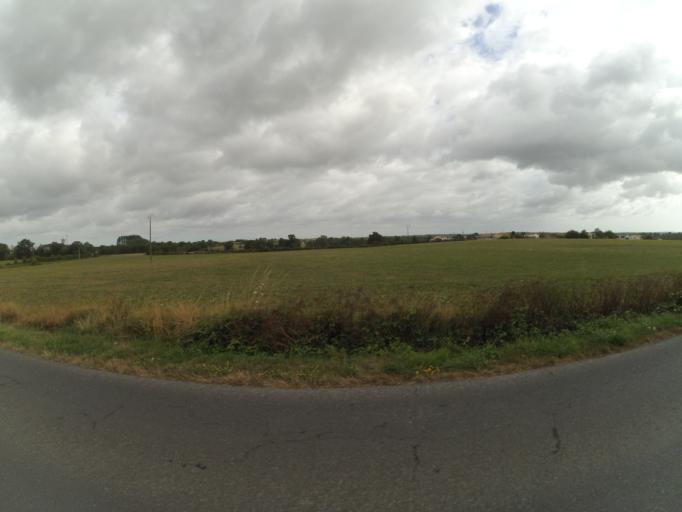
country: FR
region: Pays de la Loire
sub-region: Departement de Maine-et-Loire
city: Saint-Crespin-sur-Moine
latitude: 47.0813
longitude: -1.1720
